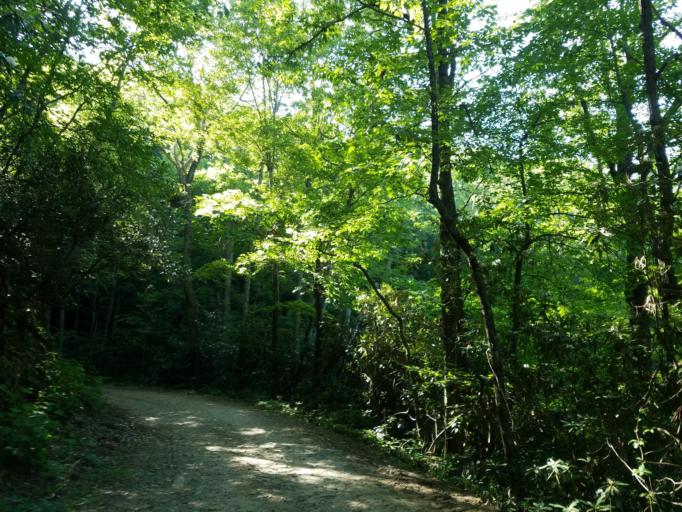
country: US
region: Georgia
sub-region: Dawson County
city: Dawsonville
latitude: 34.5883
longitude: -84.2035
